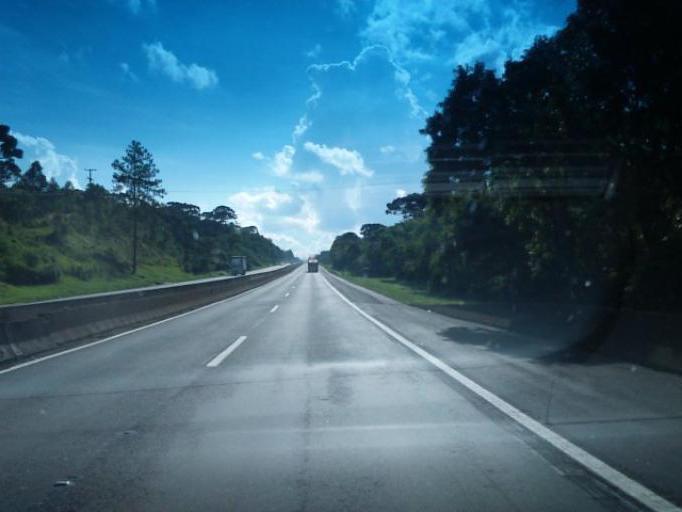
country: BR
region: Parana
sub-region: Campina Grande Do Sul
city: Campina Grande do Sul
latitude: -25.3047
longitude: -48.9703
